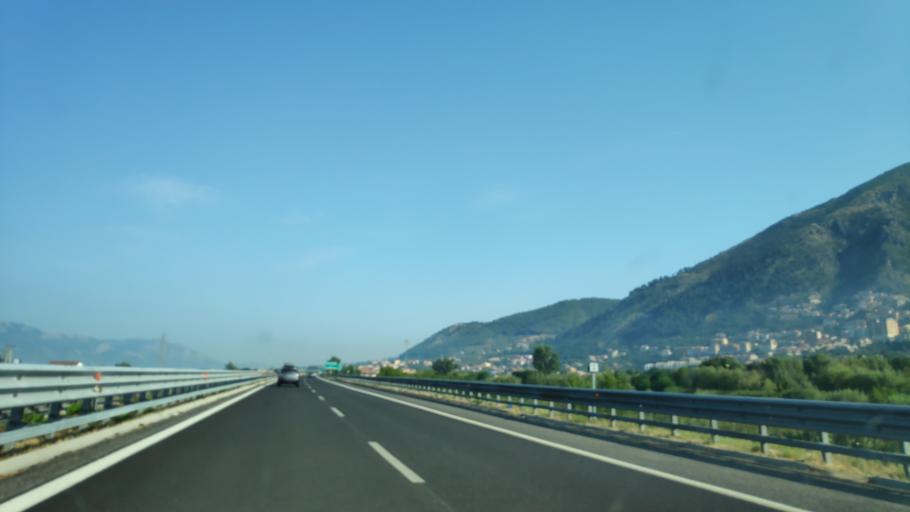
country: IT
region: Campania
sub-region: Provincia di Salerno
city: Sala Consilina
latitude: 40.3909
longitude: 15.5865
